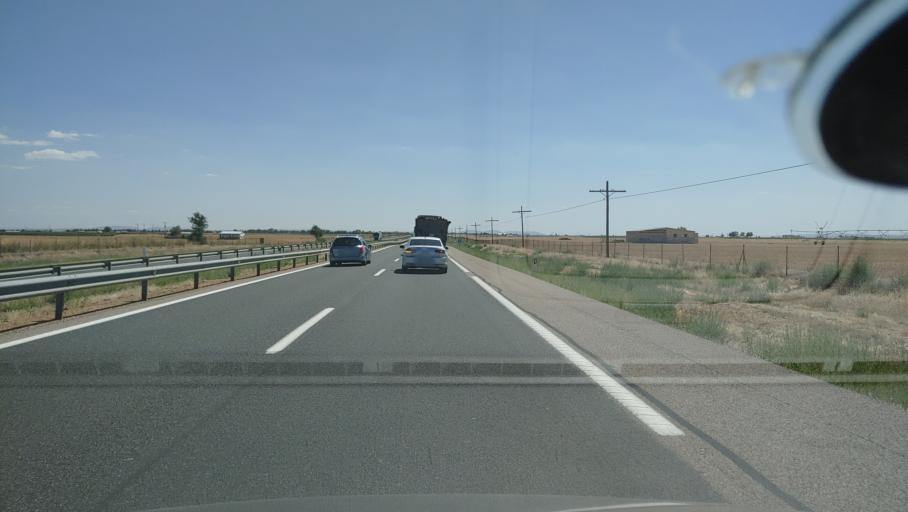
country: ES
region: Castille-La Mancha
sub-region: Provincia de Ciudad Real
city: Villarta de San Juan
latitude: 39.1501
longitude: -3.3868
